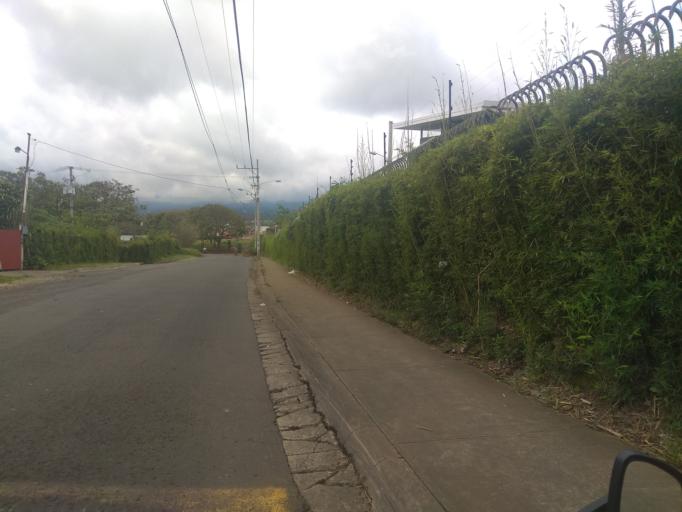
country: CR
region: Heredia
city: San Rafael
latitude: 10.0043
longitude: -84.1020
